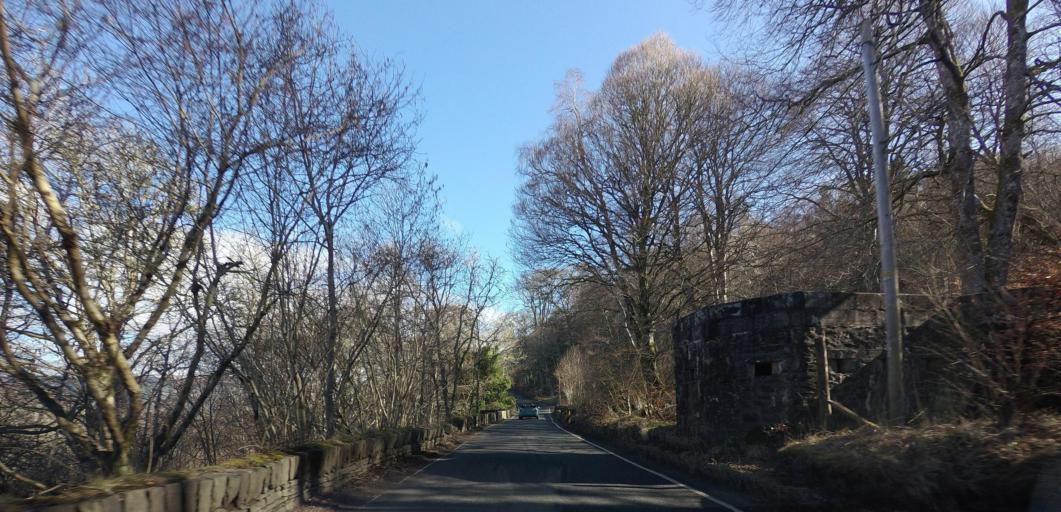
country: GB
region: Scotland
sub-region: Perth and Kinross
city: Aberfeldy
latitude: 56.5843
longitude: -3.9830
